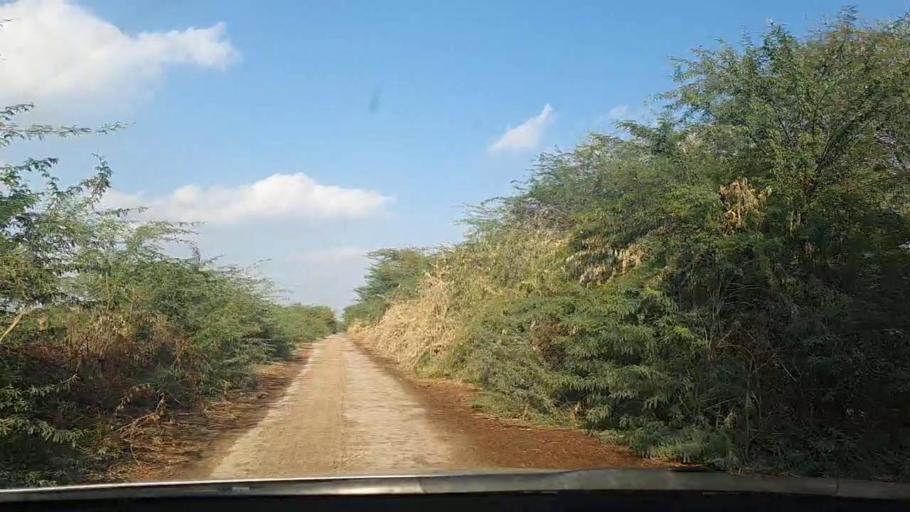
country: PK
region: Sindh
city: Tando Mittha Khan
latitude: 25.8811
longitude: 69.2944
